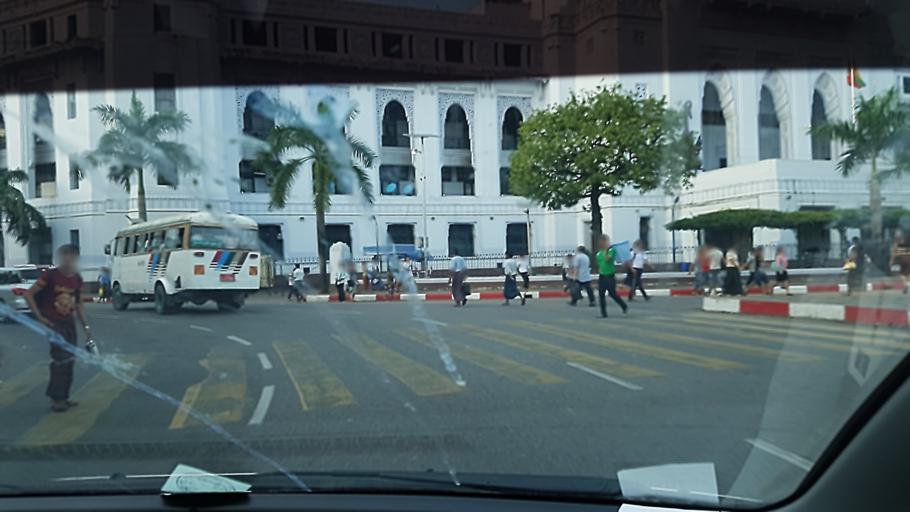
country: MM
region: Yangon
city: Yangon
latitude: 16.7743
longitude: 96.1593
